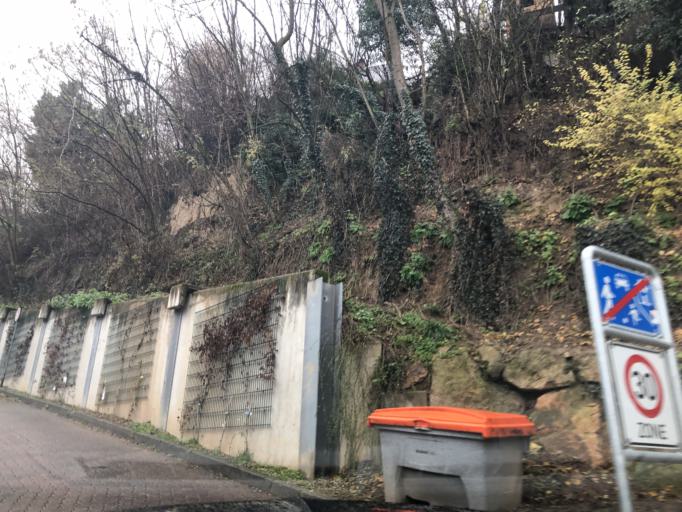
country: DE
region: Baden-Wuerttemberg
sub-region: Karlsruhe Region
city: Dossenheim
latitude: 49.4537
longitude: 8.6781
